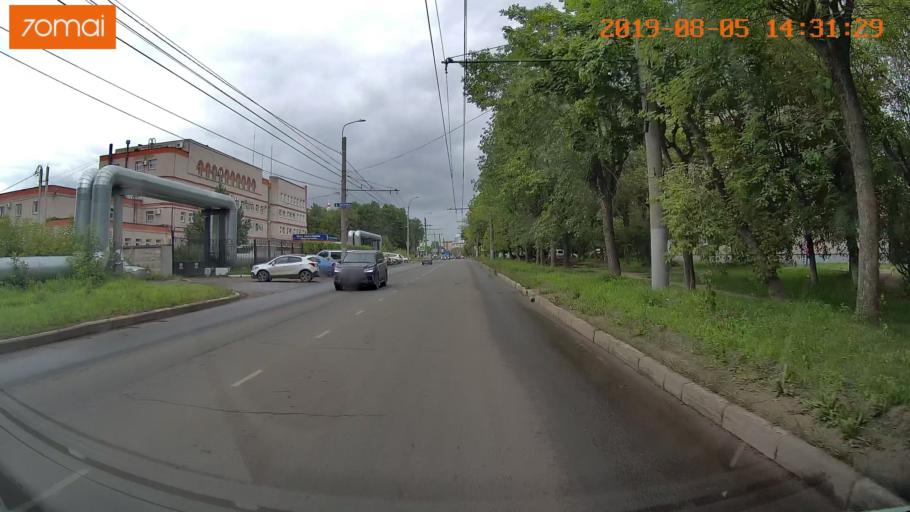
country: RU
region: Ivanovo
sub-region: Gorod Ivanovo
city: Ivanovo
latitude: 56.9871
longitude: 41.0014
